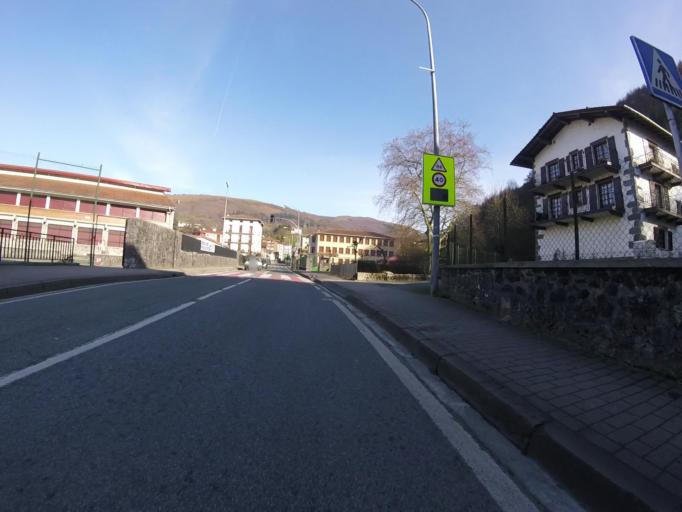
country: ES
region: Navarre
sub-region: Provincia de Navarra
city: Leitza
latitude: 43.0816
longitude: -1.9138
